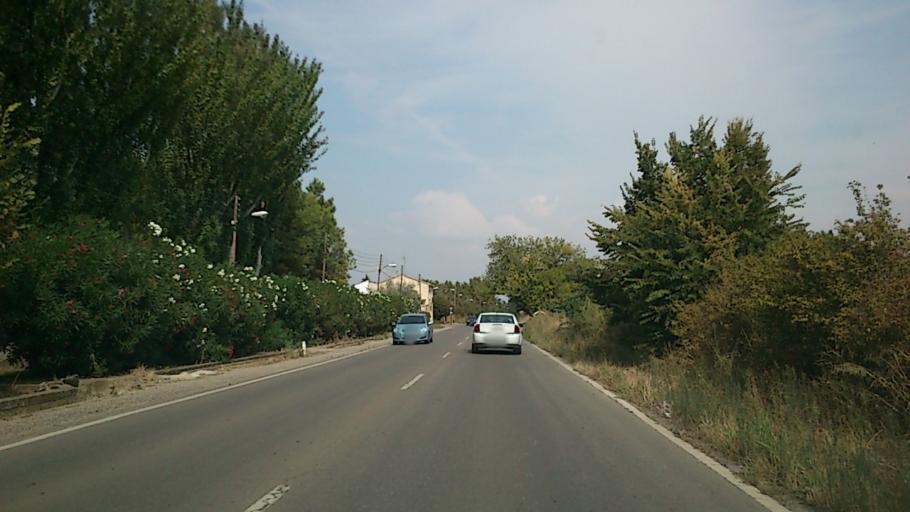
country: ES
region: Aragon
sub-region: Provincia de Zaragoza
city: Villanueva de Gallego
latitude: 41.7093
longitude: -0.8132
